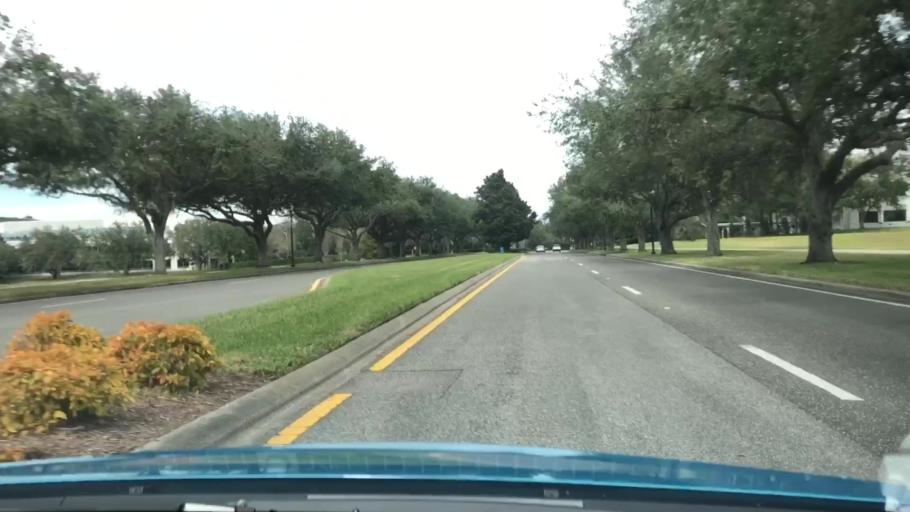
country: US
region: Florida
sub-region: Seminole County
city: Heathrow
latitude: 28.7733
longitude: -81.3588
